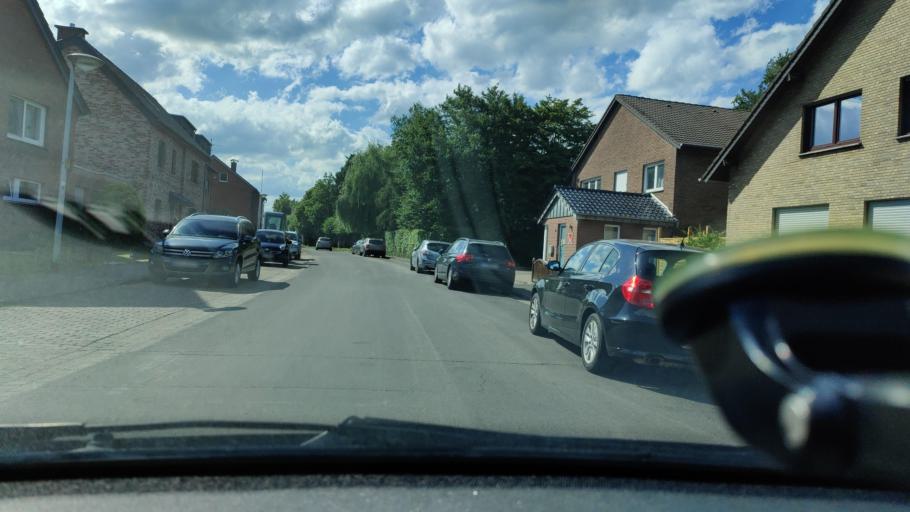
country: DE
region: North Rhine-Westphalia
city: Rheinberg
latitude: 51.5716
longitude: 6.5854
